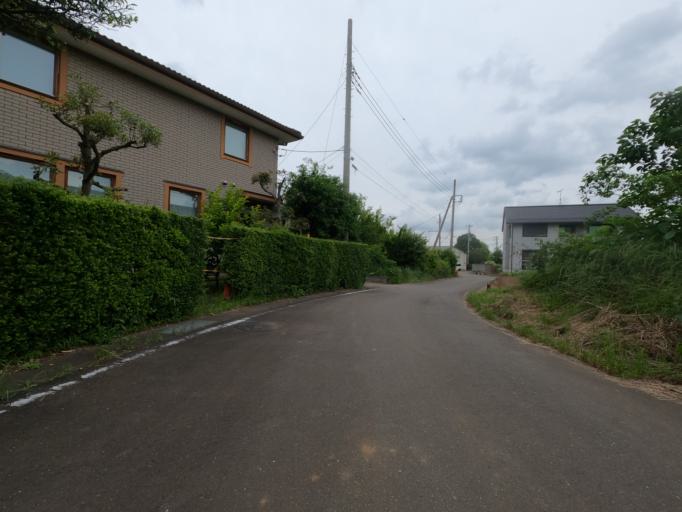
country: JP
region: Ibaraki
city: Moriya
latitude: 35.9409
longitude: 139.9718
